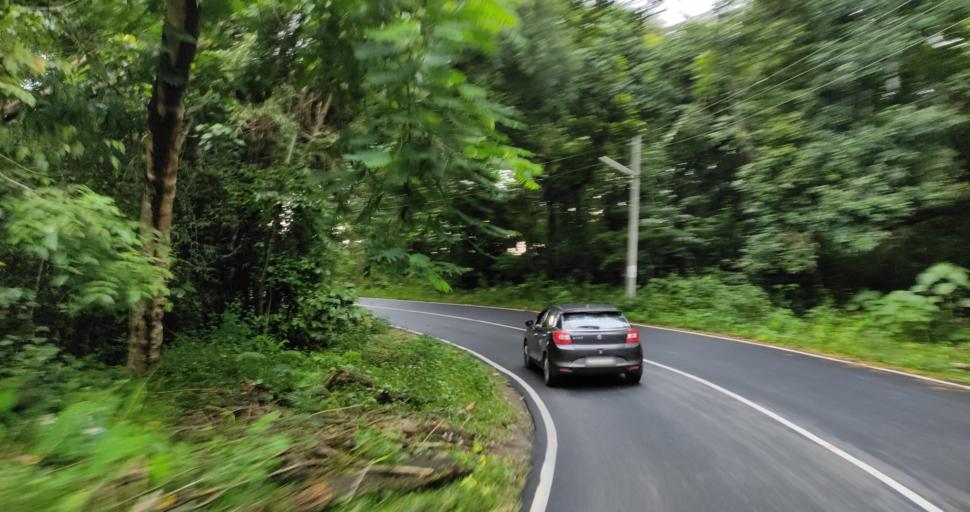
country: IN
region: Kerala
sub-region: Ernakulam
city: Angamali
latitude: 10.3002
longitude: 76.4531
